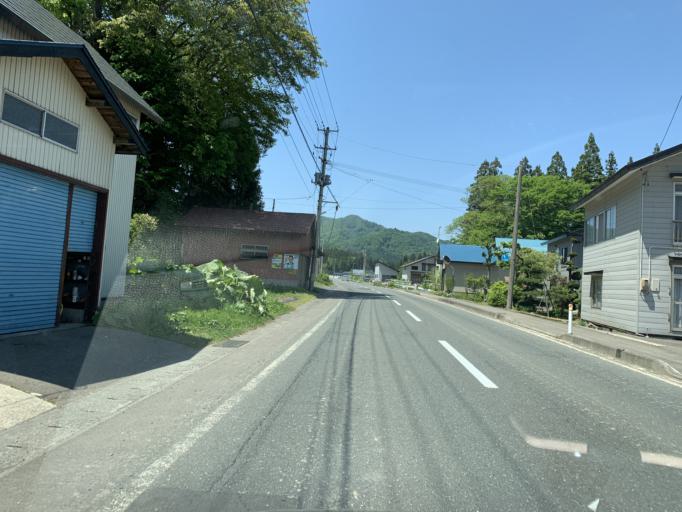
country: JP
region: Akita
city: Yokotemachi
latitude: 39.4088
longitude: 140.7509
